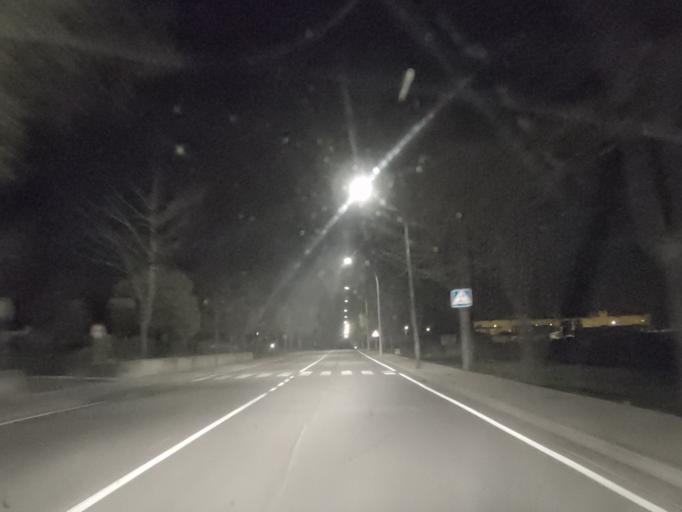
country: ES
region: Castille and Leon
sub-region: Provincia de Zamora
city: Benavente
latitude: 42.0092
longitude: -5.6864
